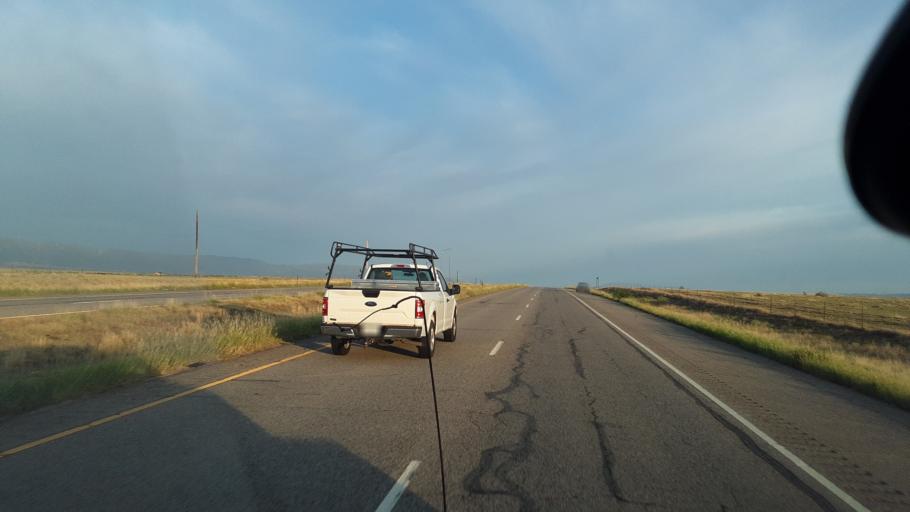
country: US
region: Colorado
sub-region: Pueblo County
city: Pueblo West
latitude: 38.3519
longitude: -104.8212
